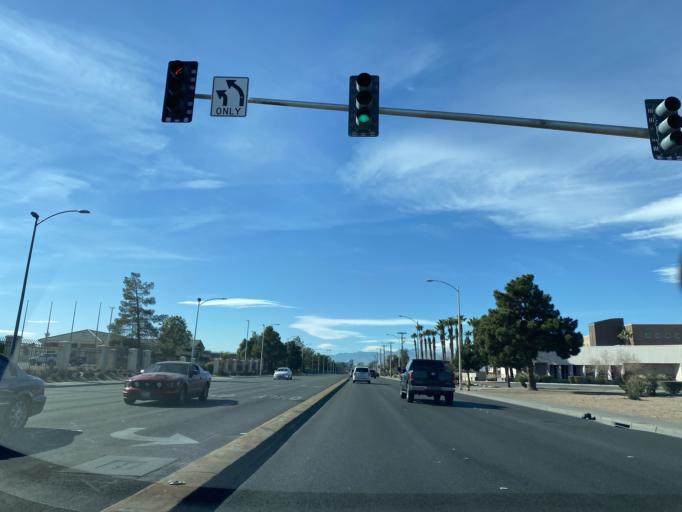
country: US
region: Nevada
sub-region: Clark County
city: North Las Vegas
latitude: 36.1735
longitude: -115.0984
